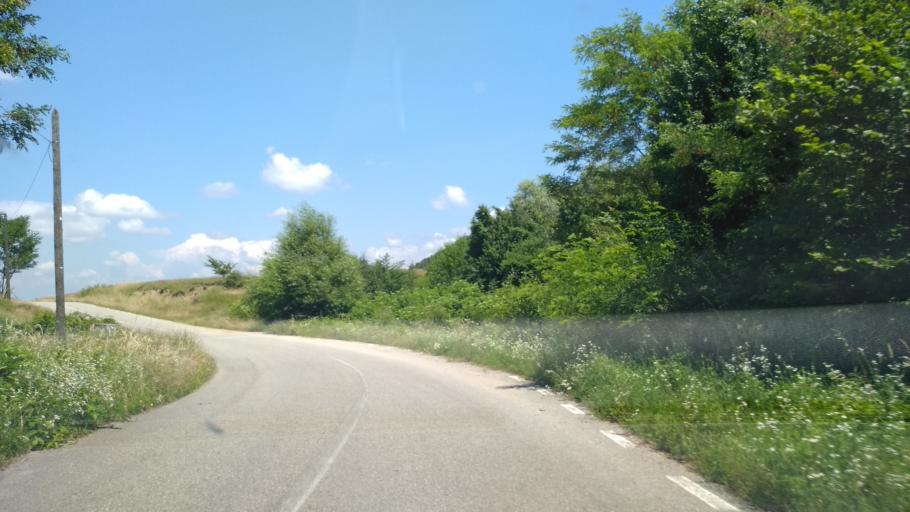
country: RO
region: Hunedoara
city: Berca
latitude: 45.6107
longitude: 23.0229
